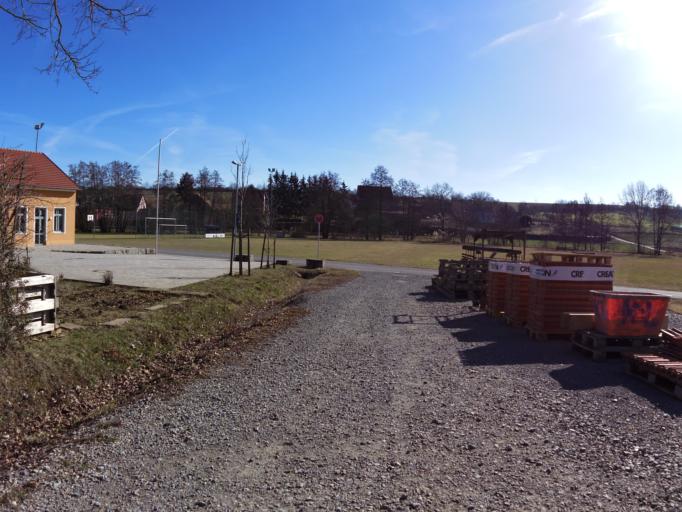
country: DE
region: Bavaria
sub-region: Regierungsbezirk Unterfranken
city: Kurnach
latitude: 49.8575
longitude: 10.0107
